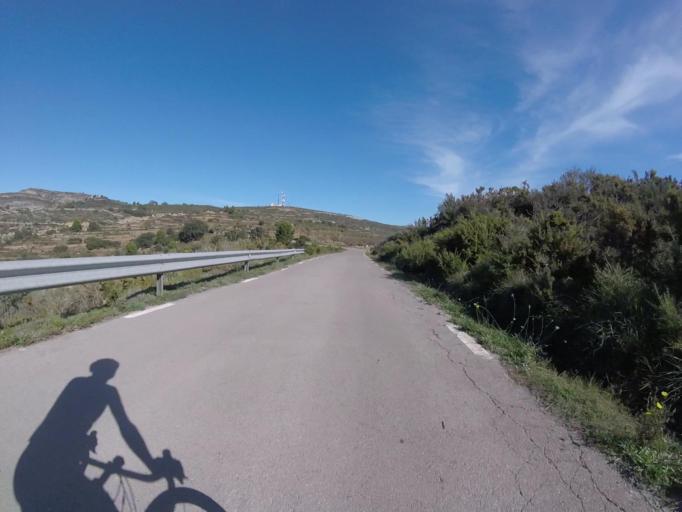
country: ES
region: Valencia
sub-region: Provincia de Castello
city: Sarratella
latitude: 40.2949
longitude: 0.0308
